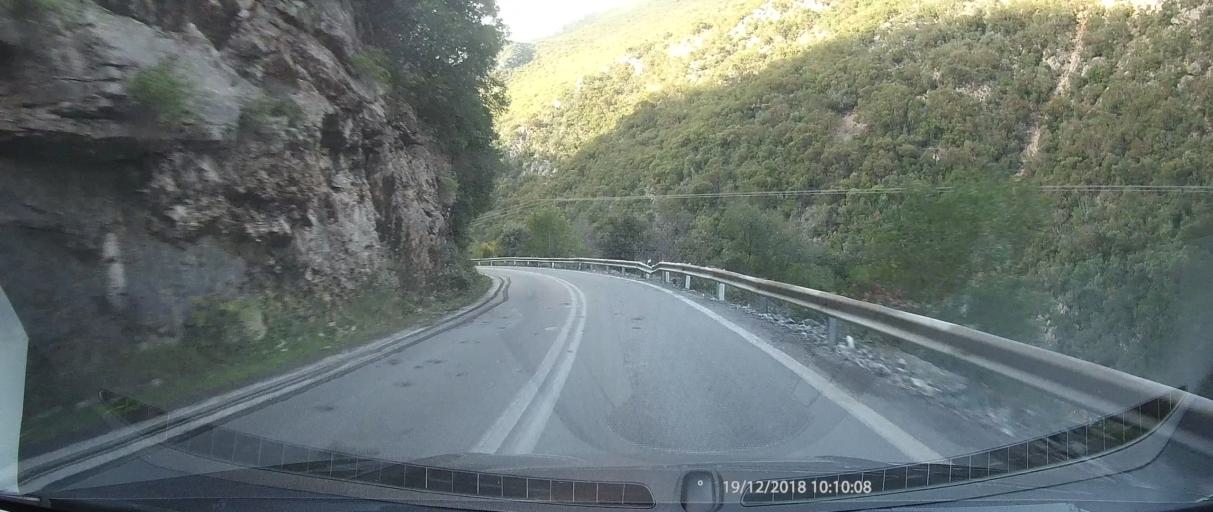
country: GR
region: Peloponnese
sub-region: Nomos Messinias
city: Kalamata
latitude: 37.1053
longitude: 22.1859
